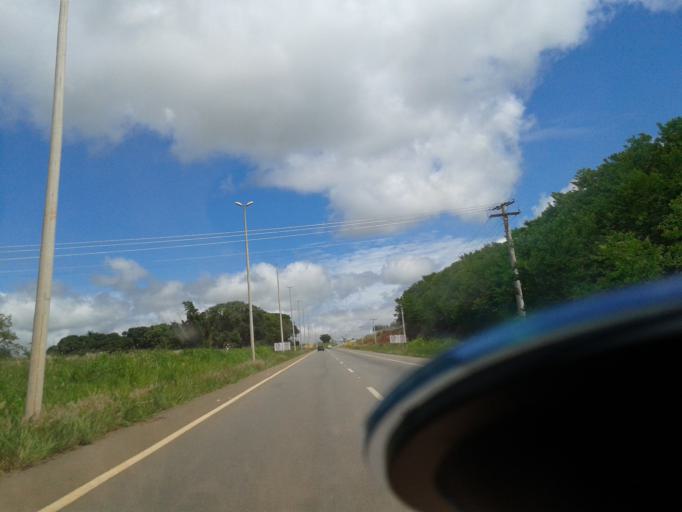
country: BR
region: Goias
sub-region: Goianira
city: Goianira
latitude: -16.4747
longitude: -49.4346
